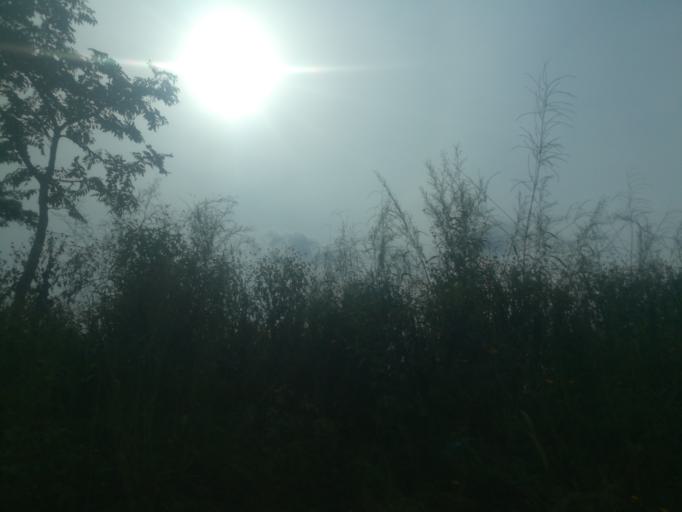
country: NG
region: Ogun
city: Ayetoro
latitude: 7.3252
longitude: 3.0682
